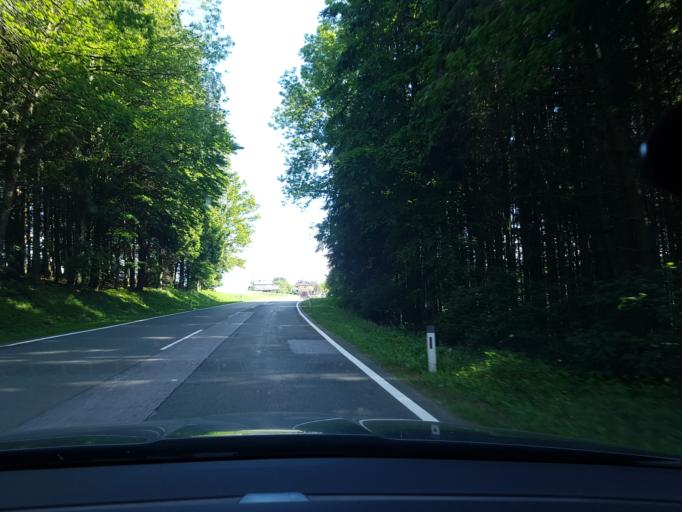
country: AT
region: Salzburg
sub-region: Politischer Bezirk Salzburg-Umgebung
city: Obertrum am See
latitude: 47.9134
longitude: 13.0827
